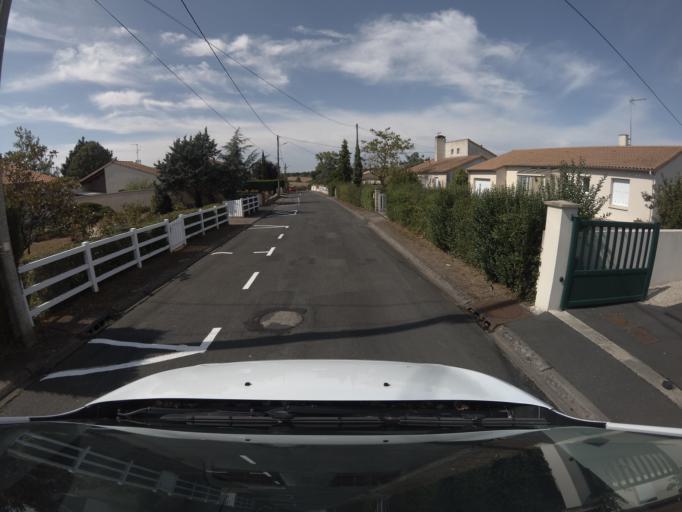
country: FR
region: Poitou-Charentes
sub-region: Departement des Deux-Sevres
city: Argenton-les-Vallees
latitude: 46.9861
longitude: -0.4549
